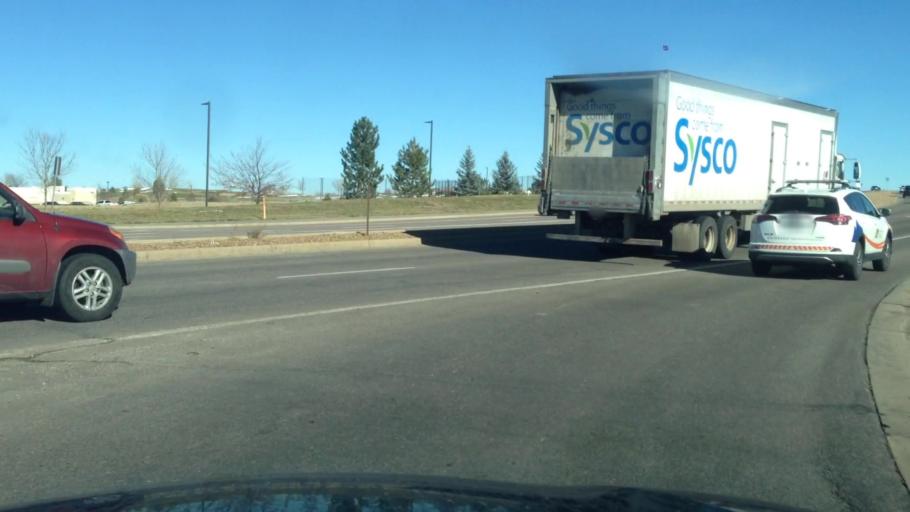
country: US
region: Colorado
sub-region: Arapahoe County
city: Centennial
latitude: 39.5873
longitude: -104.8572
